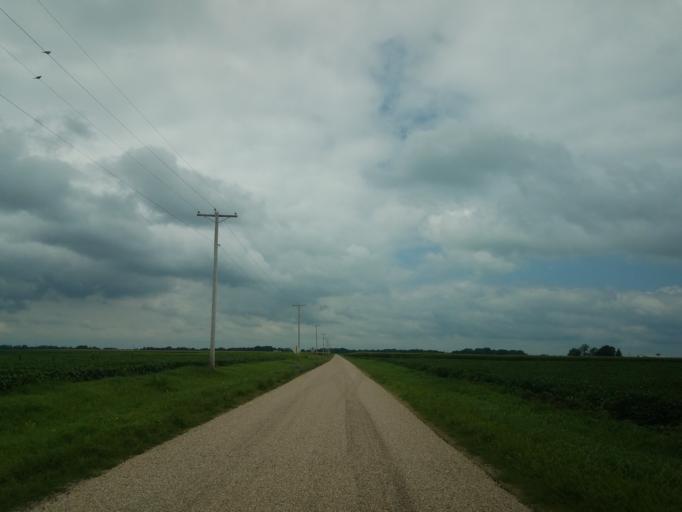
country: US
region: Illinois
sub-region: McLean County
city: Twin Grove
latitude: 40.4369
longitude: -89.0561
